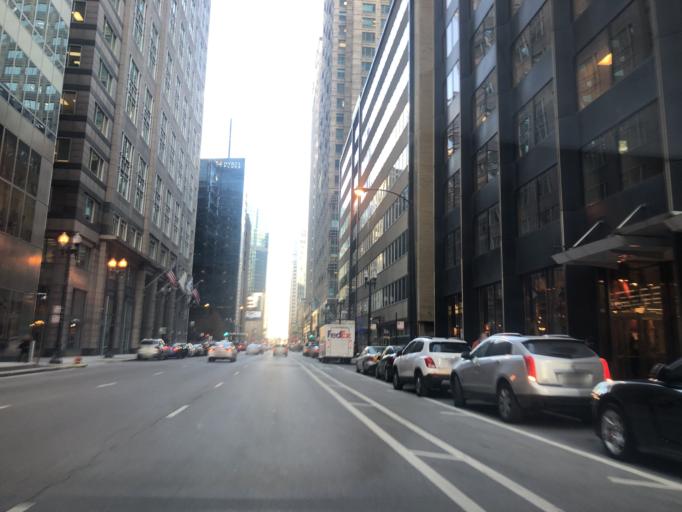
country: US
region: Illinois
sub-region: Cook County
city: Chicago
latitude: 41.8808
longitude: -87.6353
